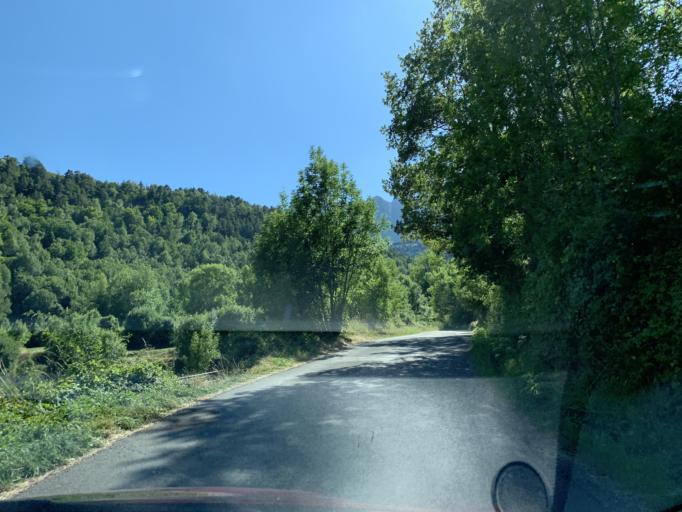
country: ES
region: Aragon
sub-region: Provincia de Huesca
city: Hoz de Jaca
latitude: 42.6942
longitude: -0.3255
